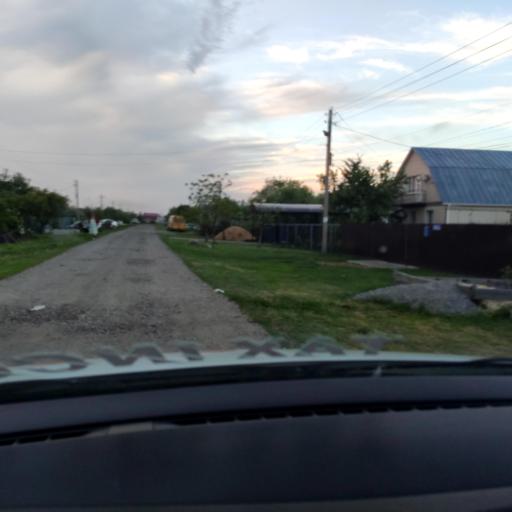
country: RU
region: Voronezj
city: Maslovka
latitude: 51.4536
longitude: 39.2376
